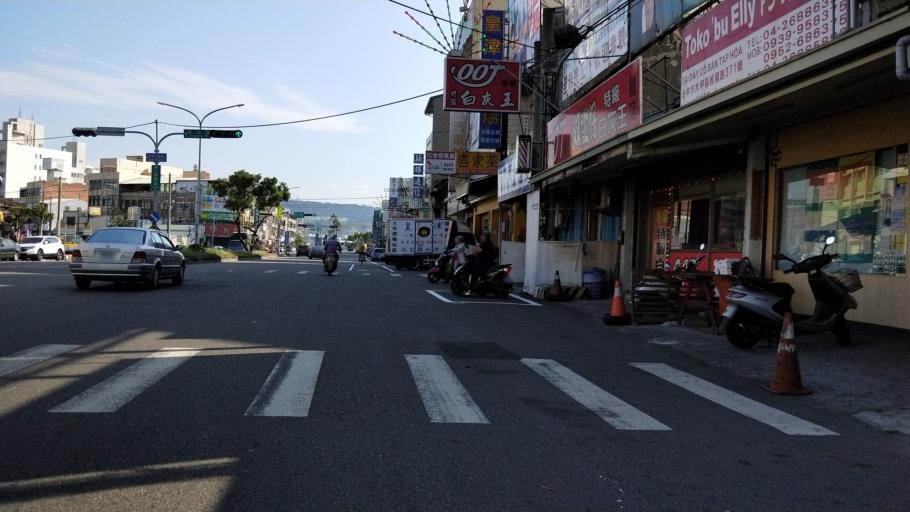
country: TW
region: Taiwan
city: Fengyuan
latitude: 24.3482
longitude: 120.6170
